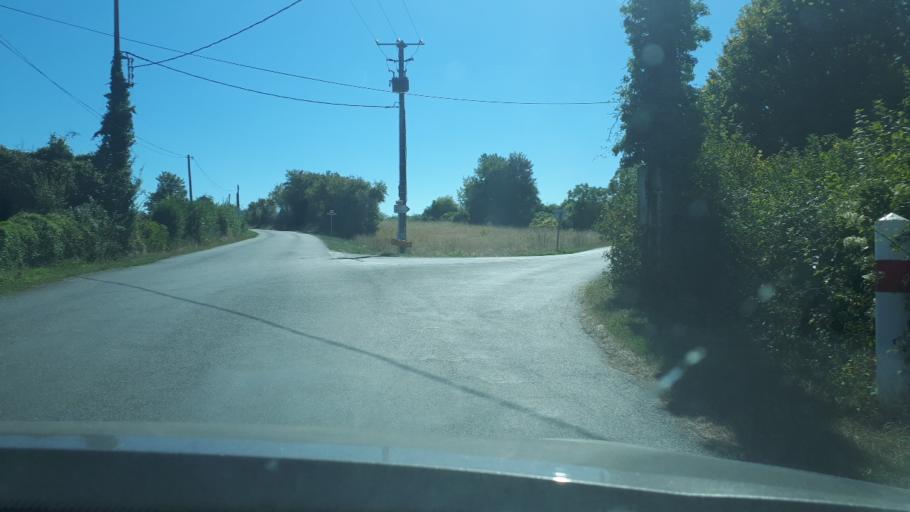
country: FR
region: Centre
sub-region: Departement du Cher
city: Sancerre
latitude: 47.2517
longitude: 2.7610
